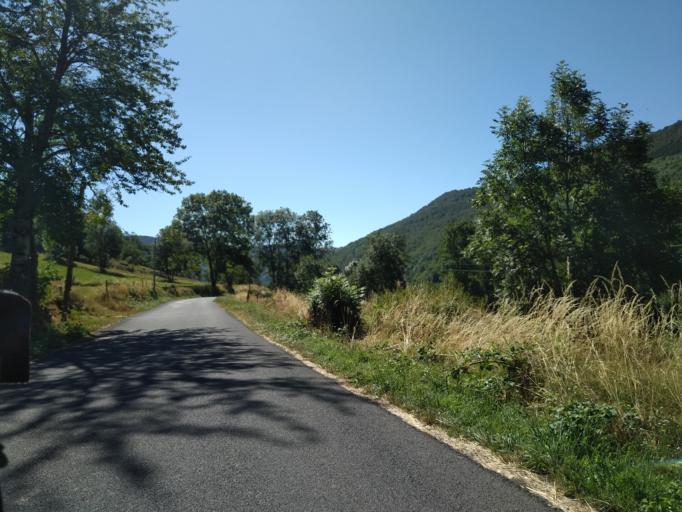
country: FR
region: Auvergne
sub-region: Departement du Cantal
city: Pierrefort
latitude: 45.0100
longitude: 2.7853
